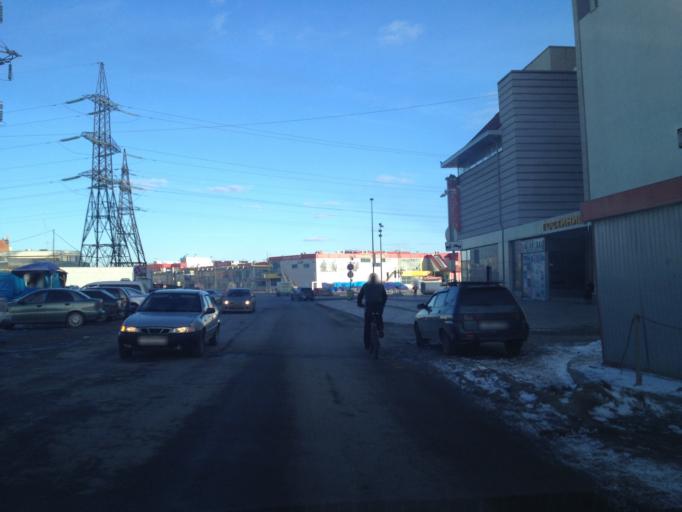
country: RU
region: Sverdlovsk
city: Yekaterinburg
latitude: 56.8619
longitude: 60.5368
